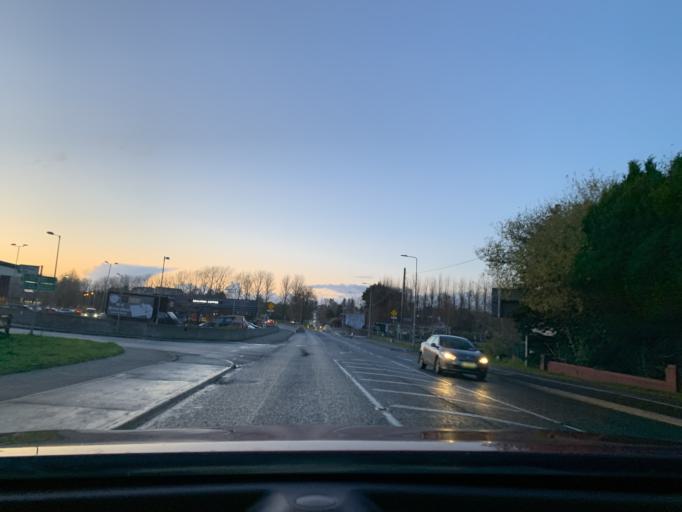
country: IE
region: Connaught
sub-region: County Leitrim
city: Carrick-on-Shannon
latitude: 53.9458
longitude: -8.0763
